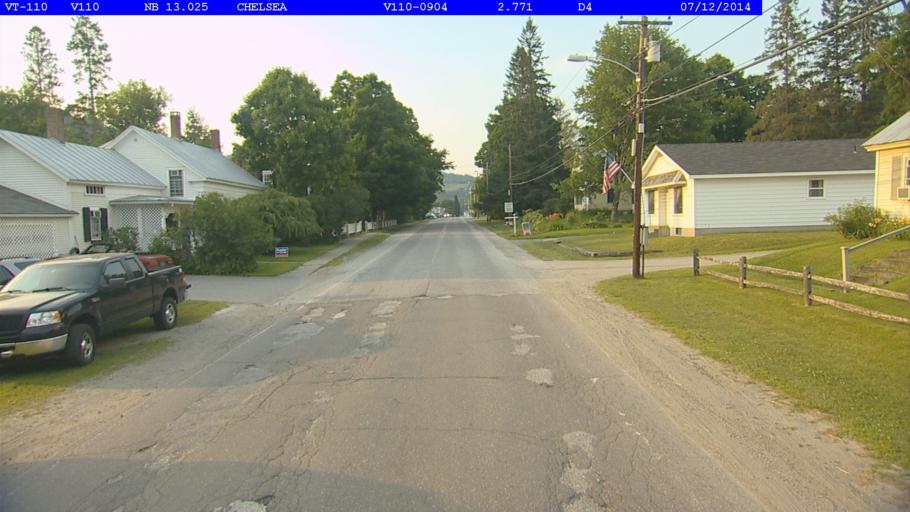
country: US
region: Vermont
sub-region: Orange County
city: Chelsea
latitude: 43.9863
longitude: -72.4481
